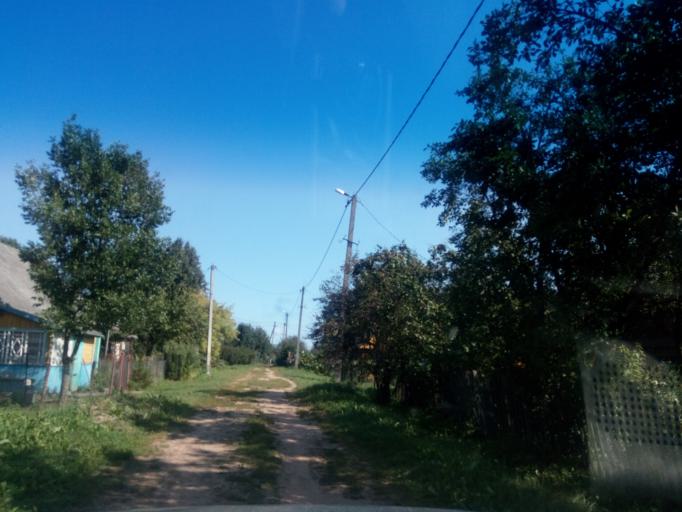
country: BY
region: Vitebsk
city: Dzisna
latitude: 55.6697
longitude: 28.3269
